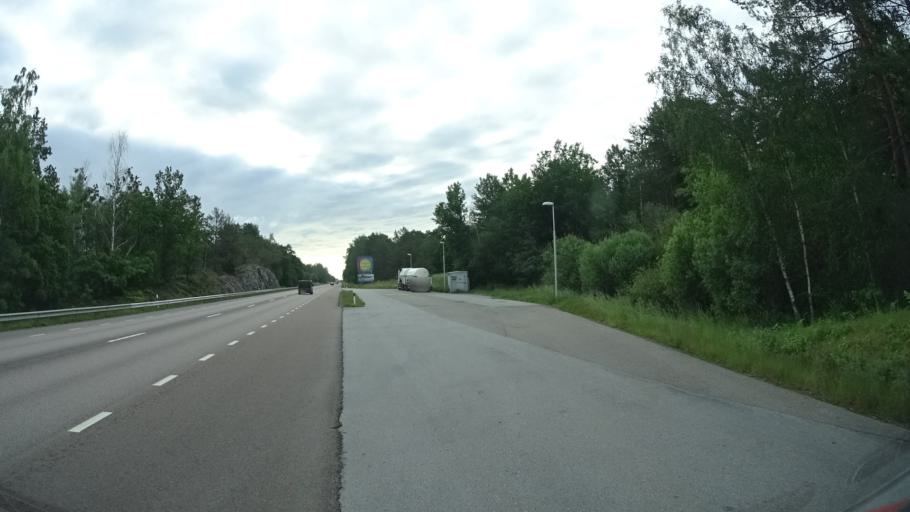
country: SE
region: Kalmar
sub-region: Oskarshamns Kommun
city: Oskarshamn
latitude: 57.2616
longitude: 16.3895
